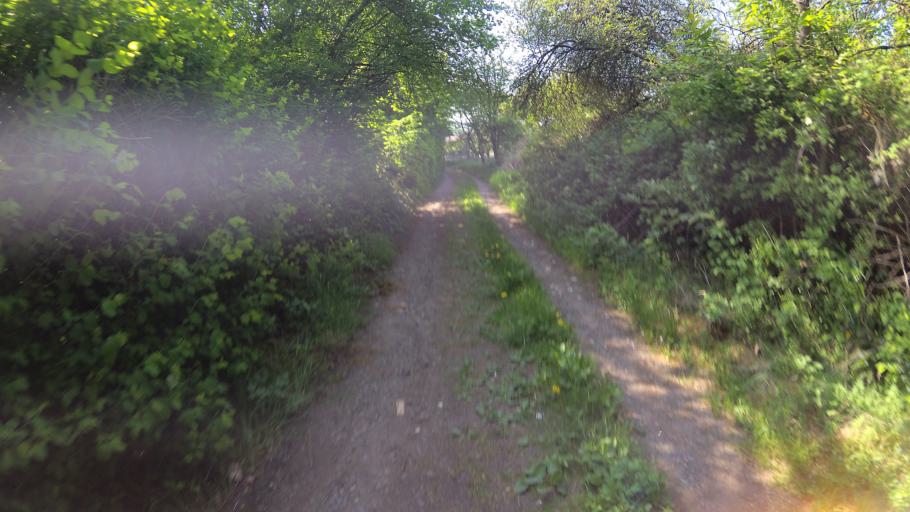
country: DE
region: Saarland
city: Merchweiler
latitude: 49.3533
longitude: 7.0508
